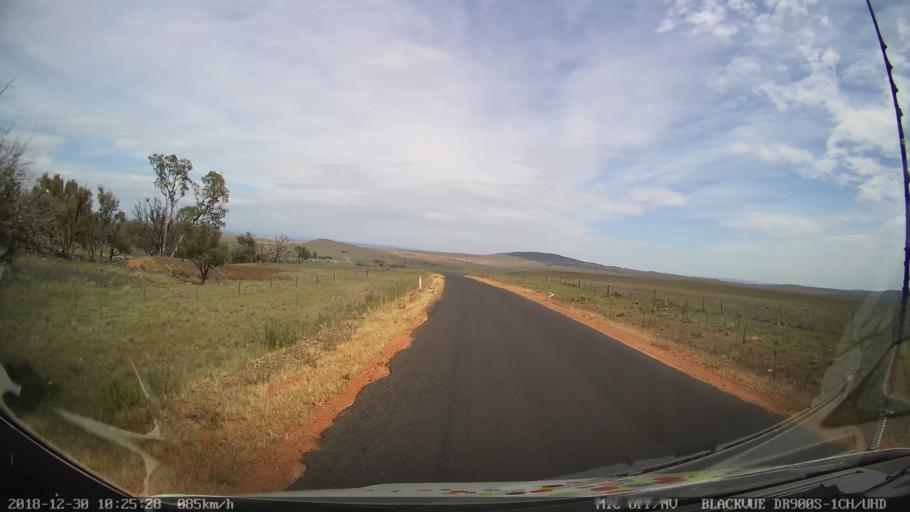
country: AU
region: New South Wales
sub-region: Snowy River
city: Berridale
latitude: -36.5241
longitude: 148.9588
